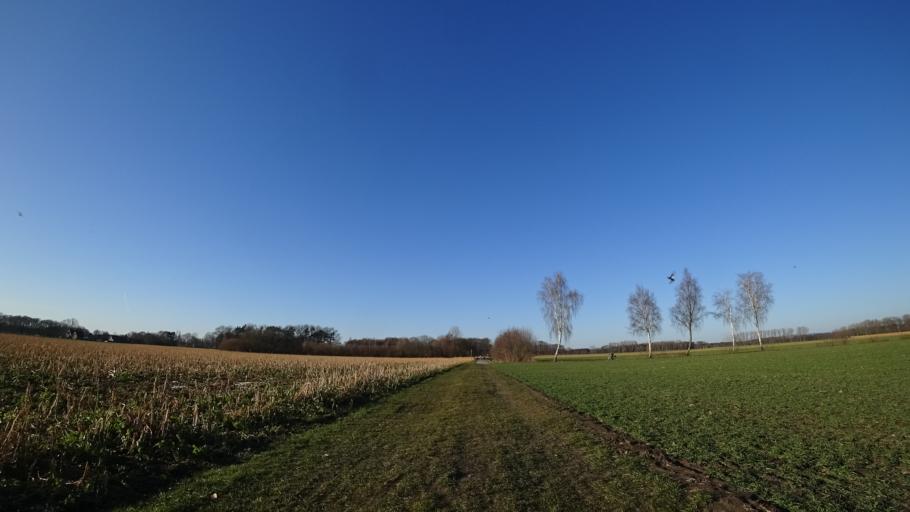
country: DE
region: North Rhine-Westphalia
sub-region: Regierungsbezirk Detmold
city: Guetersloh
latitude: 51.9349
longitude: 8.3251
